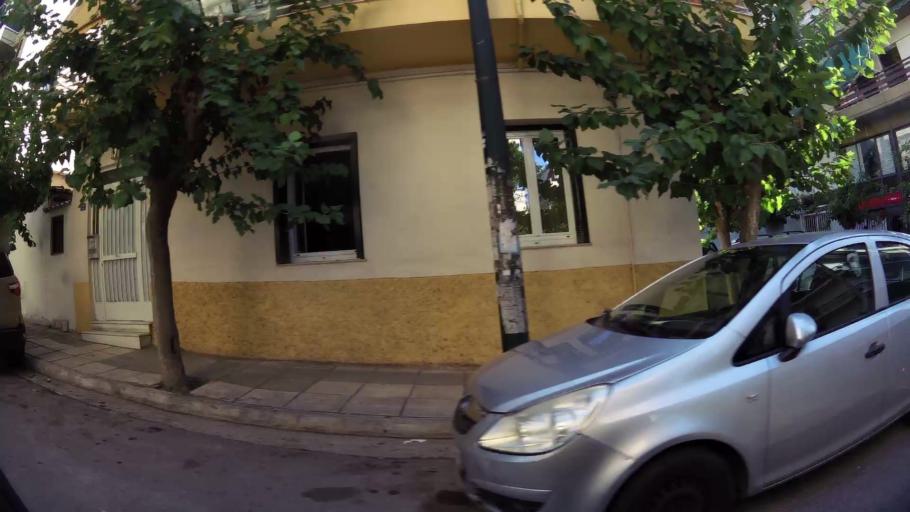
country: GR
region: Attica
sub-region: Nomarchia Athinas
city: Galatsi
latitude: 38.0222
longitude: 23.7455
